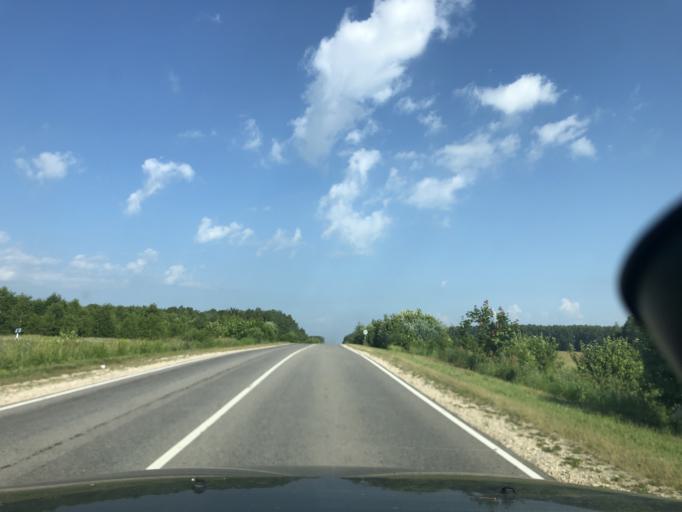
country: RU
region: Tula
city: Dubna
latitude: 54.1342
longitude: 37.0254
